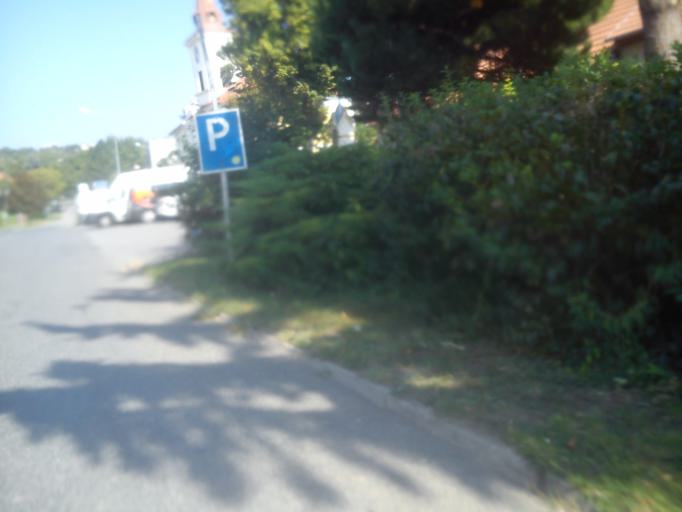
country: CZ
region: South Moravian
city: Sokolnice
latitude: 49.1037
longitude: 16.7557
